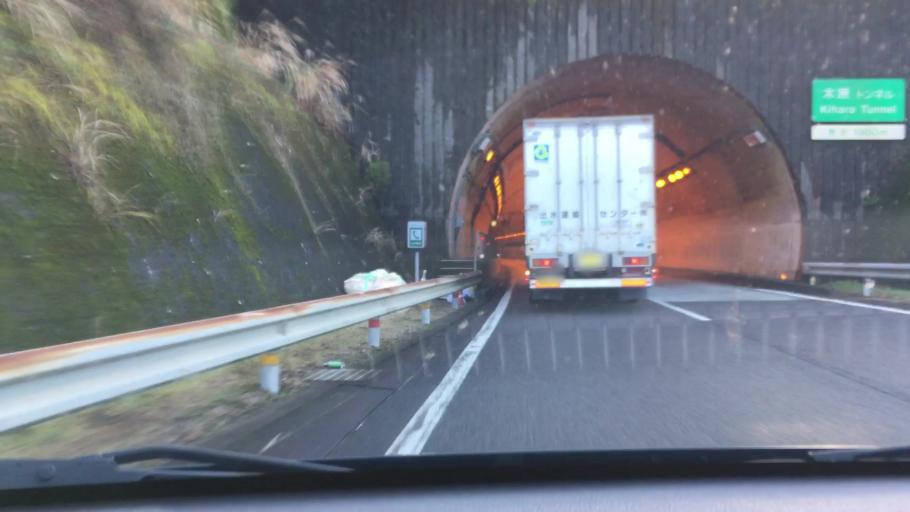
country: JP
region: Kagoshima
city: Okuchi-shinohara
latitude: 31.9827
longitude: 130.7513
